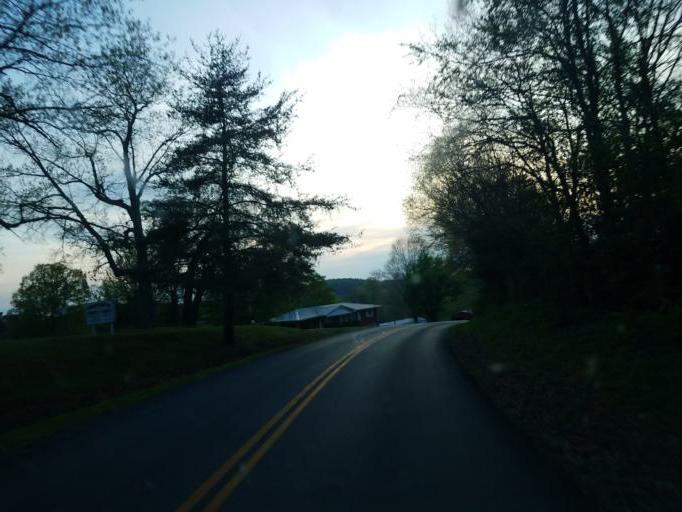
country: US
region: Kentucky
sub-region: Hart County
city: Munfordville
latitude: 37.2410
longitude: -85.7416
